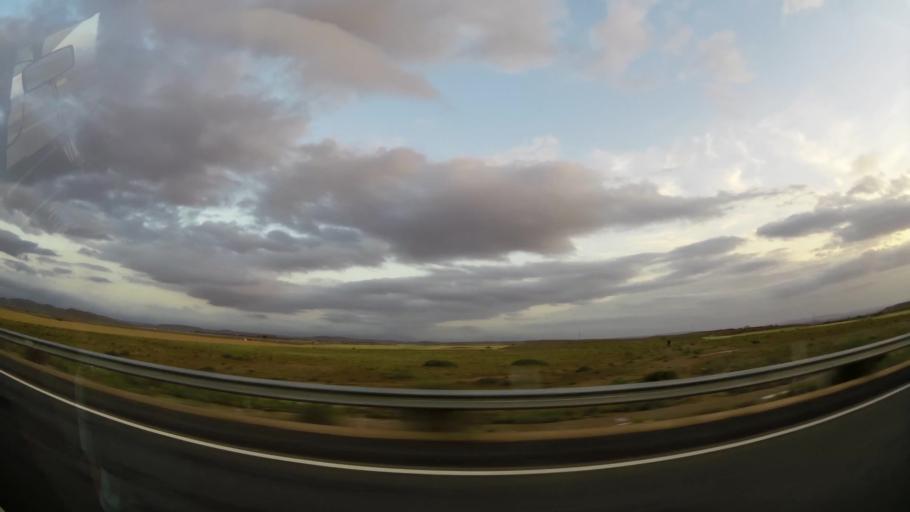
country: MA
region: Oriental
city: Taourirt
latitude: 34.6050
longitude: -2.7538
